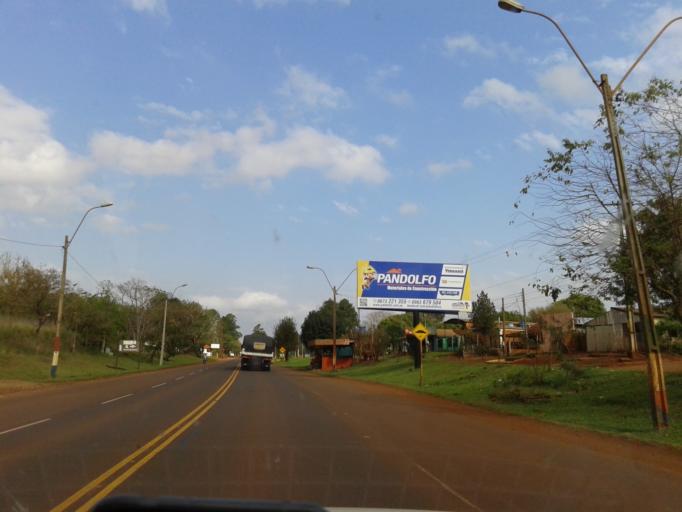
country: PY
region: Itapua
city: Arquitecto Tomas Romero Pereira
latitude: -26.4921
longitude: -55.2800
